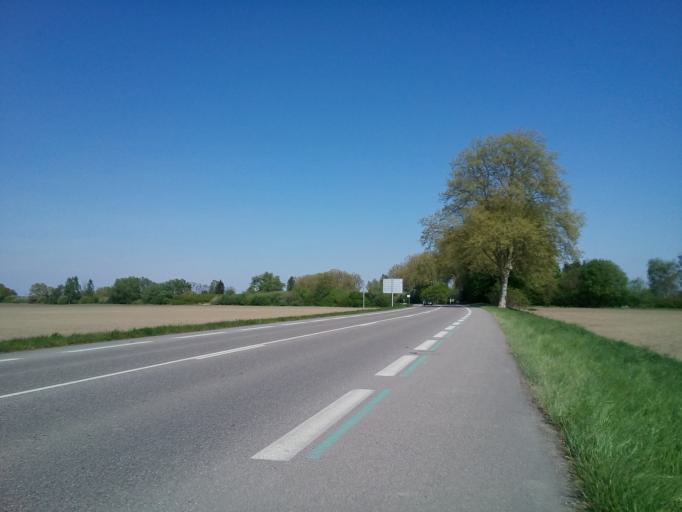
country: FR
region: Alsace
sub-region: Departement du Bas-Rhin
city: La Wantzenau
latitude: 48.6507
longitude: 7.8059
